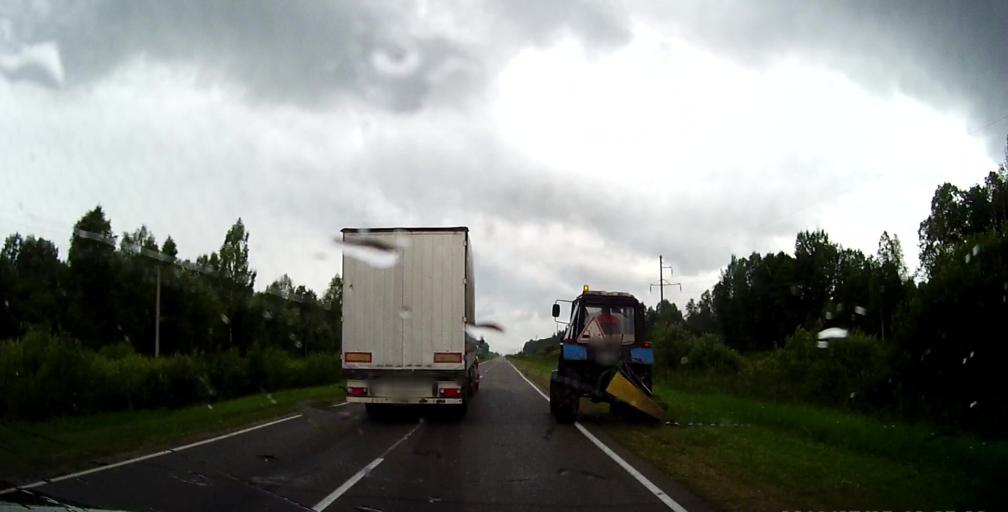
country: RU
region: Smolensk
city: Demidov
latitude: 55.2083
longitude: 31.4938
